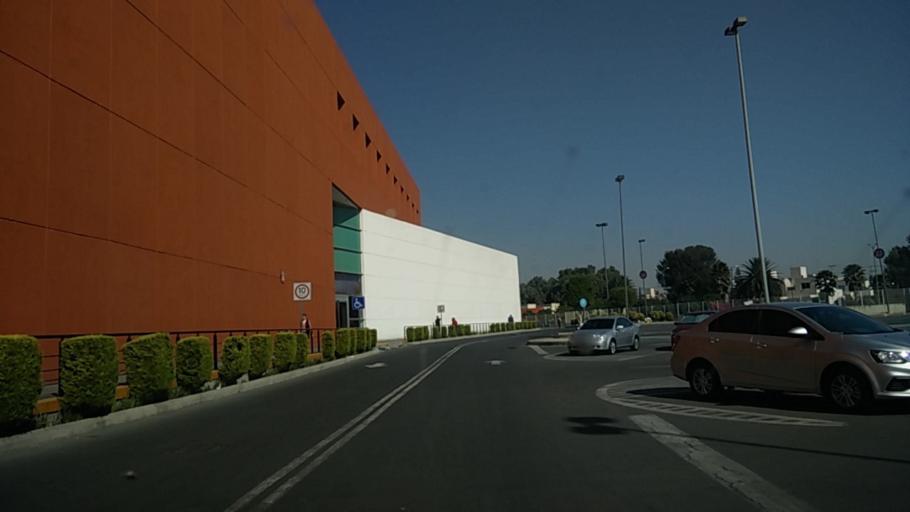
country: MX
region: Mexico
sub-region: Atenco
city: Colonia el Salado
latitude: 19.5849
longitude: -99.0230
